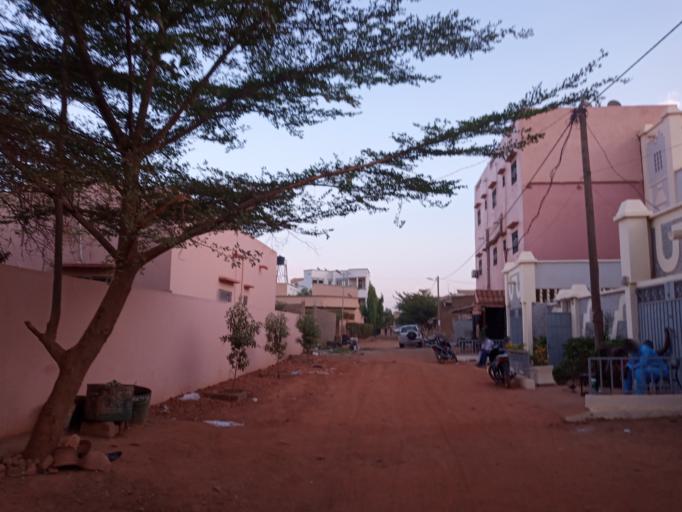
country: ML
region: Bamako
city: Bamako
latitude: 12.5695
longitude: -7.9849
